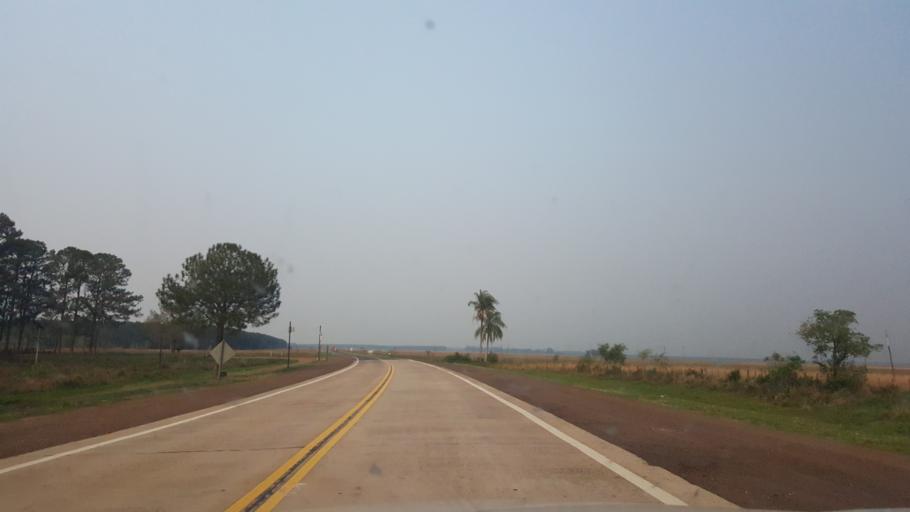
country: AR
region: Corrientes
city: Ituzaingo
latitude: -27.6326
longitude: -56.9027
